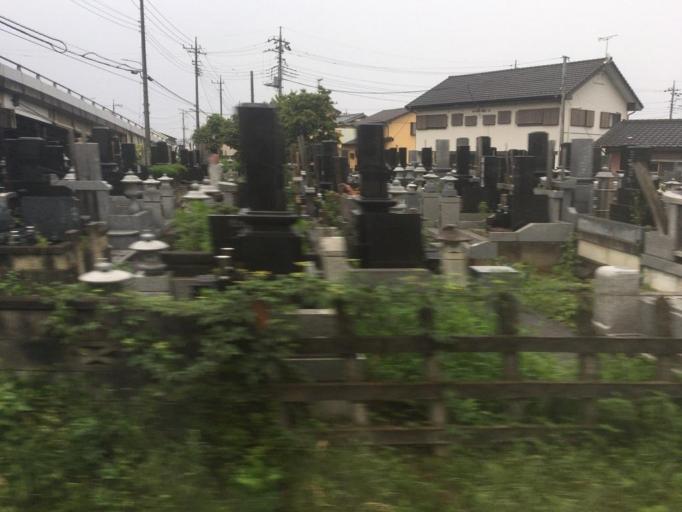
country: JP
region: Gunma
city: Ota
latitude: 36.2891
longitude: 139.3583
